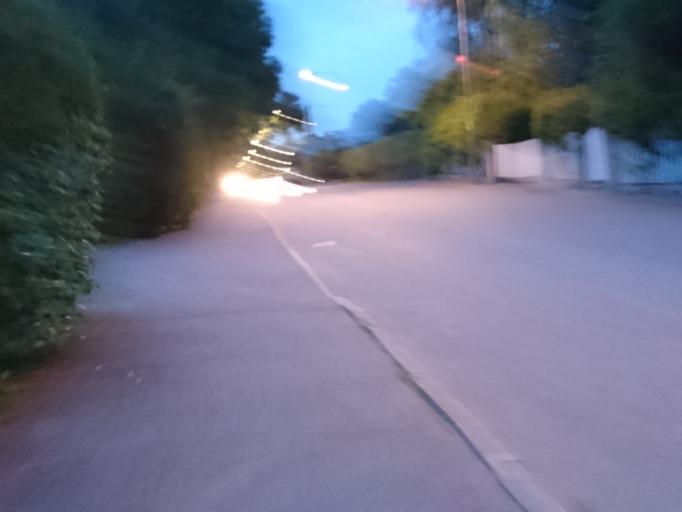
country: SE
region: Stockholm
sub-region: Huddinge Kommun
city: Huddinge
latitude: 59.2750
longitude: 17.9948
